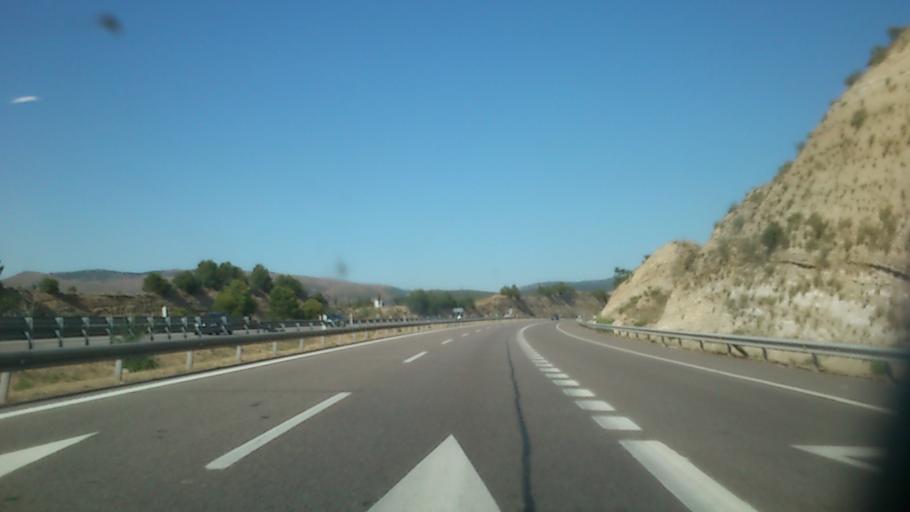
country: ES
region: Aragon
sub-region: Provincia de Zaragoza
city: Calatayud
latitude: 41.3558
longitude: -1.6136
